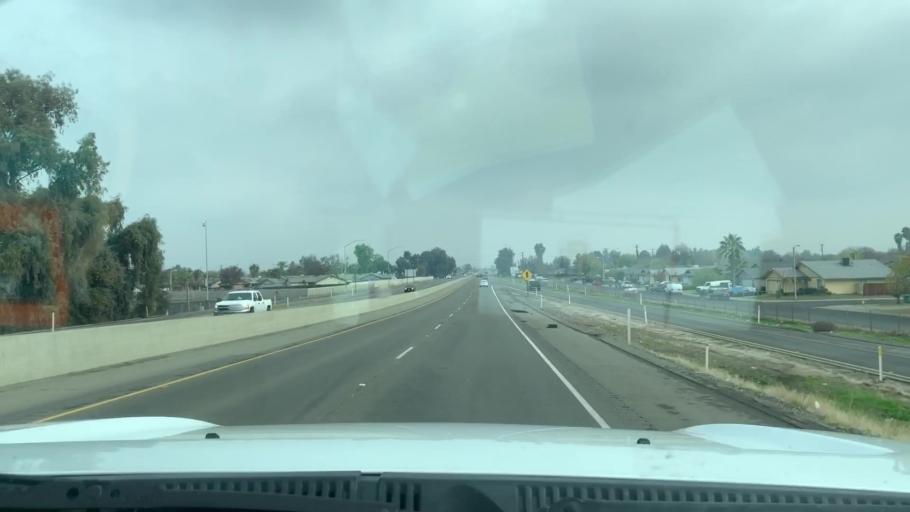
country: US
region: California
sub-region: Kings County
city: Armona
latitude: 36.3096
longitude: -119.7067
